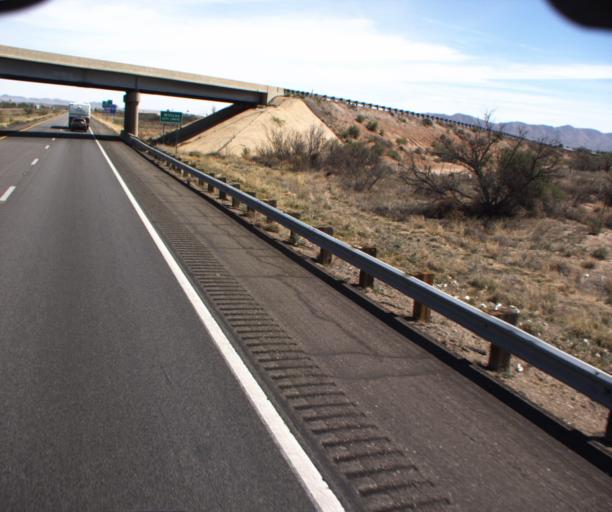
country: US
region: Arizona
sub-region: Cochise County
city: Willcox
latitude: 32.2532
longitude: -109.8540
